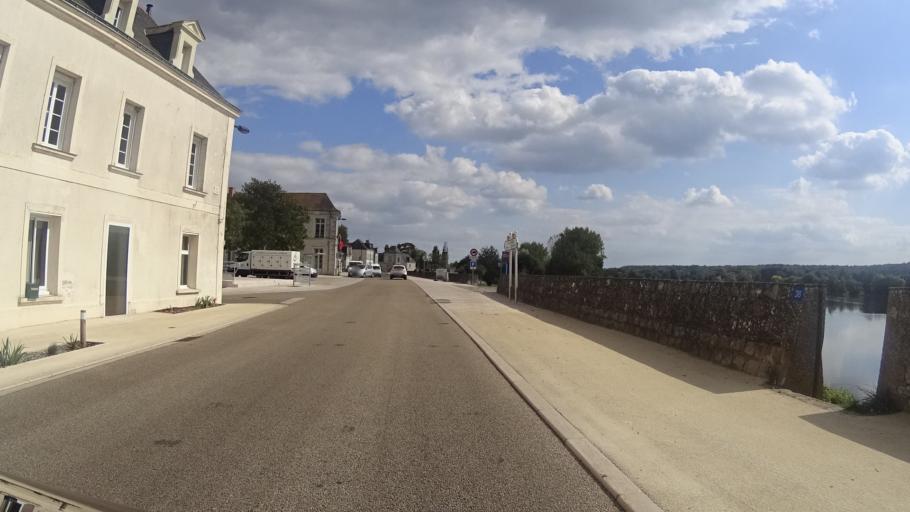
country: FR
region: Pays de la Loire
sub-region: Departement de Maine-et-Loire
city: Saint-Clement-des-Levees
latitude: 47.3307
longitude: -0.1855
